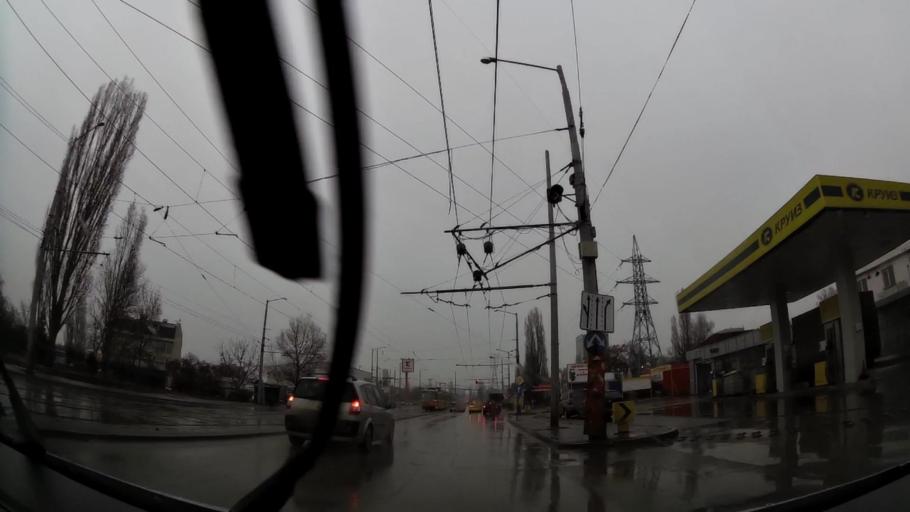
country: BG
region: Sofia-Capital
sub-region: Stolichna Obshtina
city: Sofia
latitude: 42.6742
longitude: 23.3800
